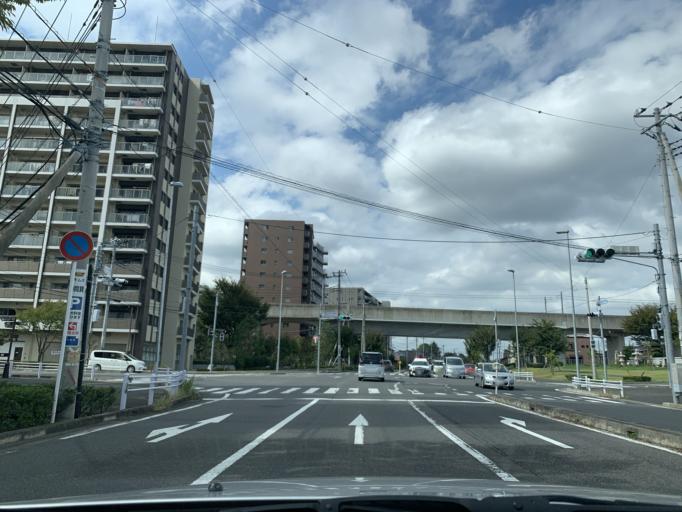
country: JP
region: Chiba
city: Nagareyama
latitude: 35.8741
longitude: 139.9291
